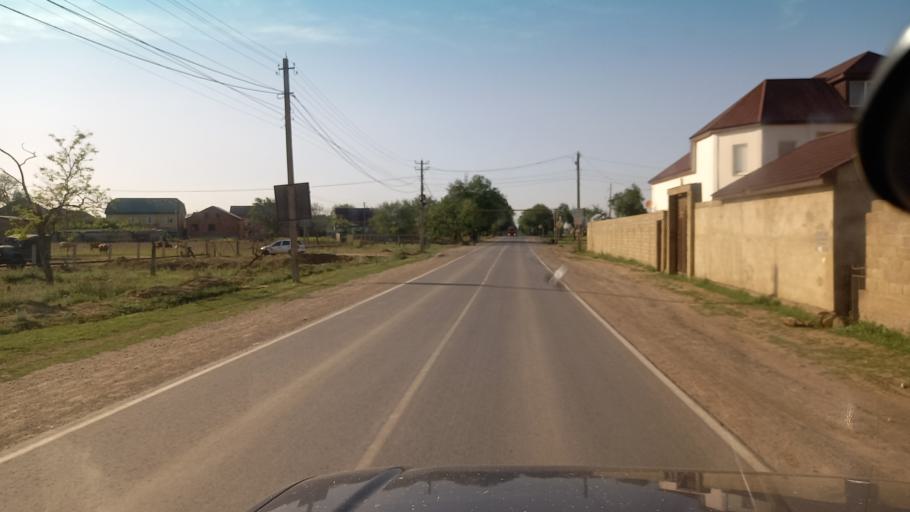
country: RU
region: Dagestan
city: Shamkhal-Termen
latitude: 43.0094
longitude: 47.3315
